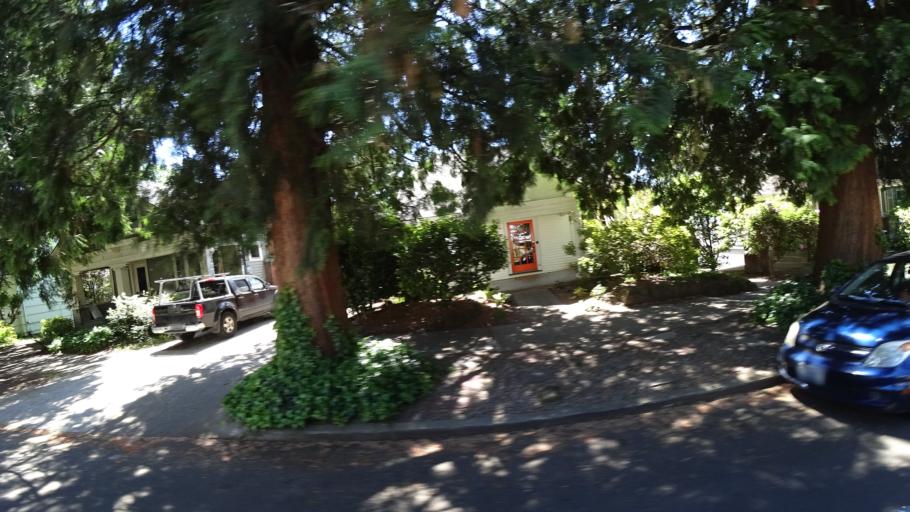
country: US
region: Oregon
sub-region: Multnomah County
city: Portland
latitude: 45.5019
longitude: -122.6231
